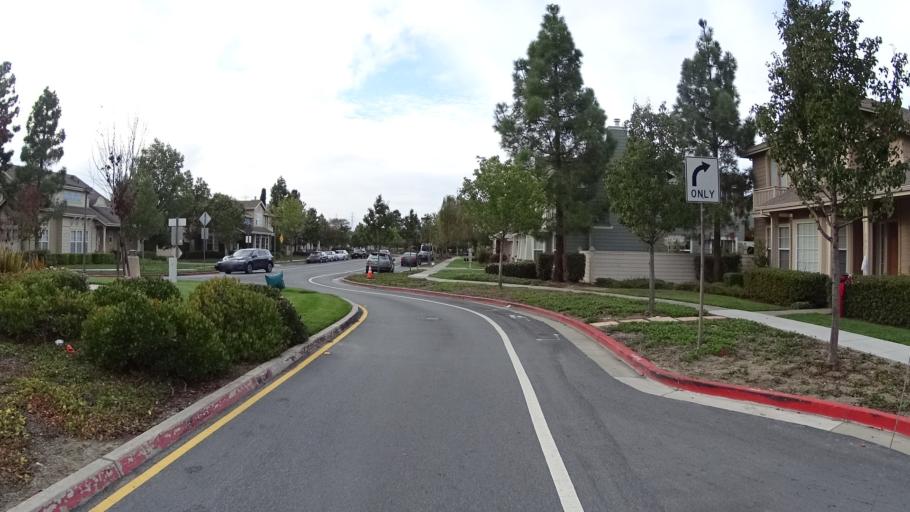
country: US
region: California
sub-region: San Mateo County
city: Redwood Shores
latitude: 37.5461
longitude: -122.2383
